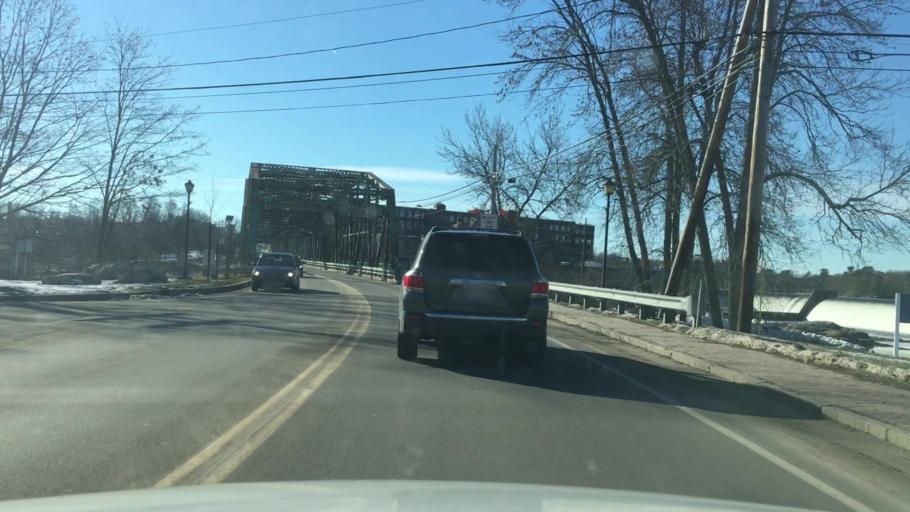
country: US
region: Maine
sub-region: Cumberland County
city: Brunswick
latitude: 43.9226
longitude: -69.9652
